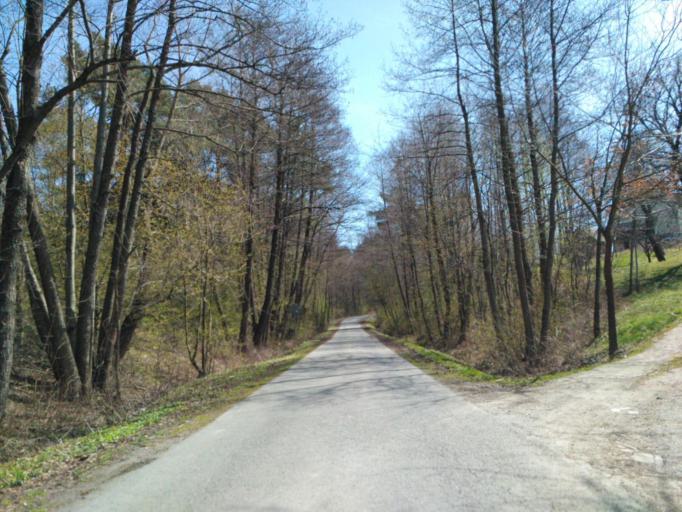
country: PL
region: Subcarpathian Voivodeship
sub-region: Powiat strzyzowski
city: Babica
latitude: 49.9265
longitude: 21.8856
